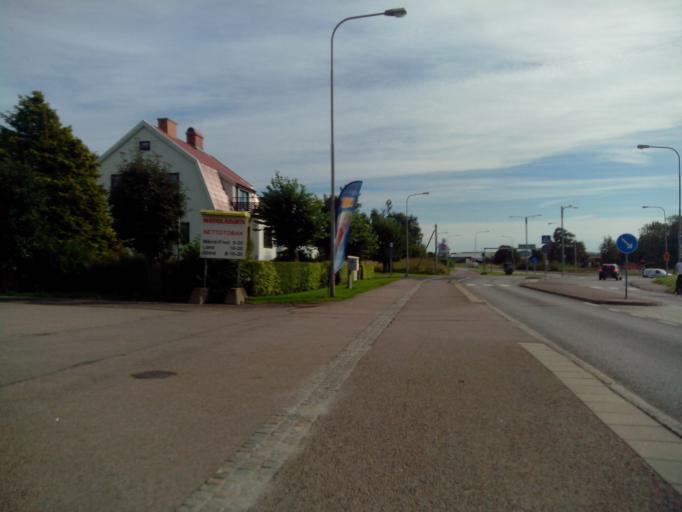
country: SE
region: Vaestra Goetaland
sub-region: Goteborg
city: Goeteborg
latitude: 57.7312
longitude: 11.9594
